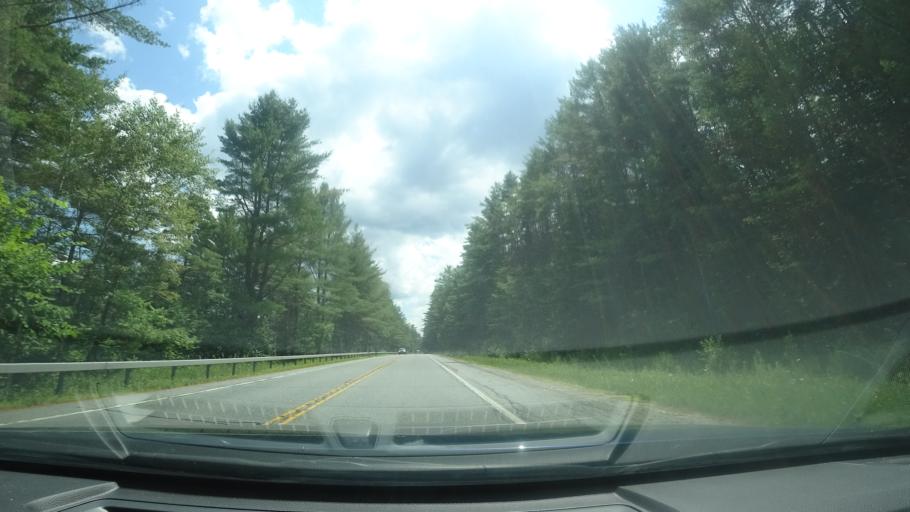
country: US
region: New York
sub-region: Warren County
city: Warrensburg
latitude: 43.5309
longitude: -73.7932
